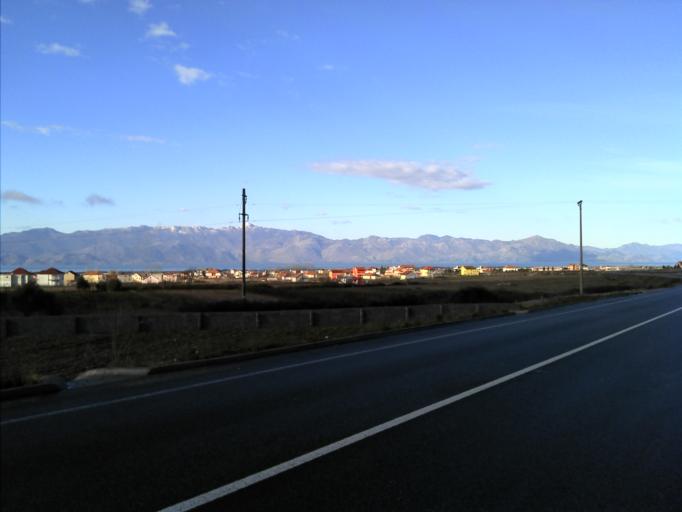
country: AL
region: Shkoder
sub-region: Rrethi i Malesia e Madhe
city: Koplik
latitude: 42.2219
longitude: 19.4407
